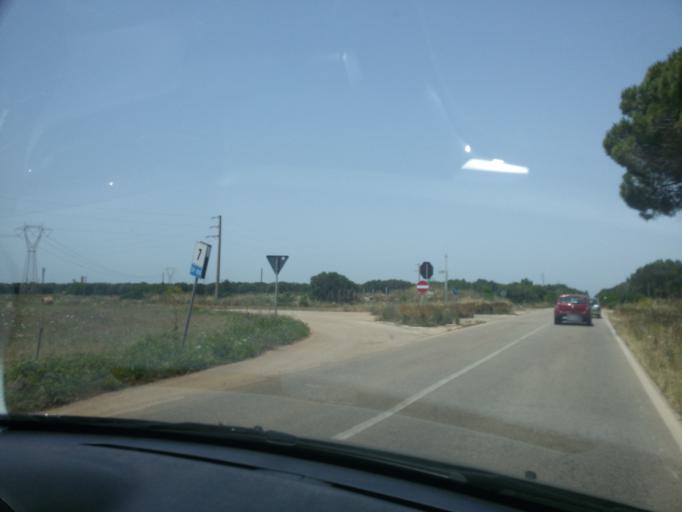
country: IT
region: Apulia
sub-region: Provincia di Brindisi
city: San Pancrazio Salentino
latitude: 40.3451
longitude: 17.8475
